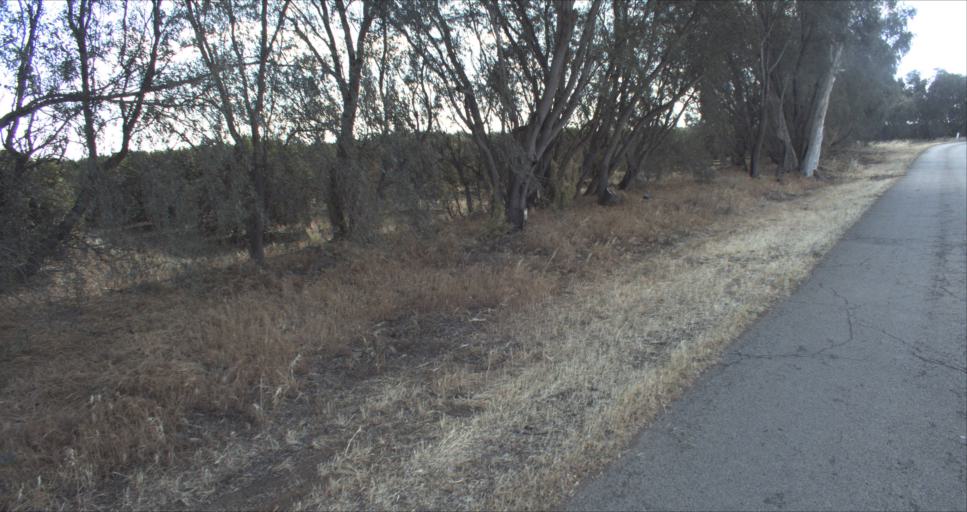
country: AU
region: New South Wales
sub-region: Leeton
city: Leeton
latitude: -34.5124
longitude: 146.2323
